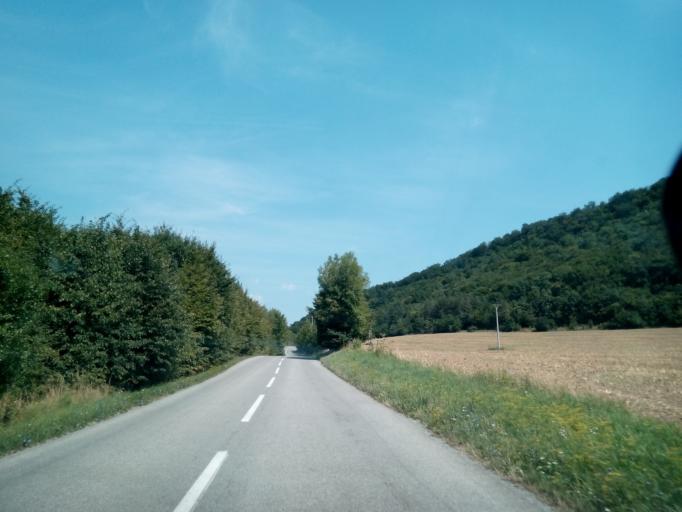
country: SK
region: Kosicky
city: Kosice
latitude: 48.8511
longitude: 21.2270
